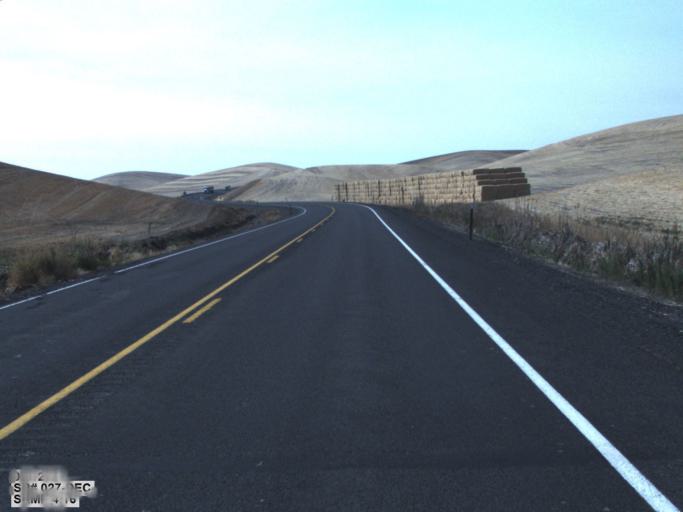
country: US
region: Washington
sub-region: Whitman County
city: Pullman
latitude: 46.7843
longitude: -117.1493
